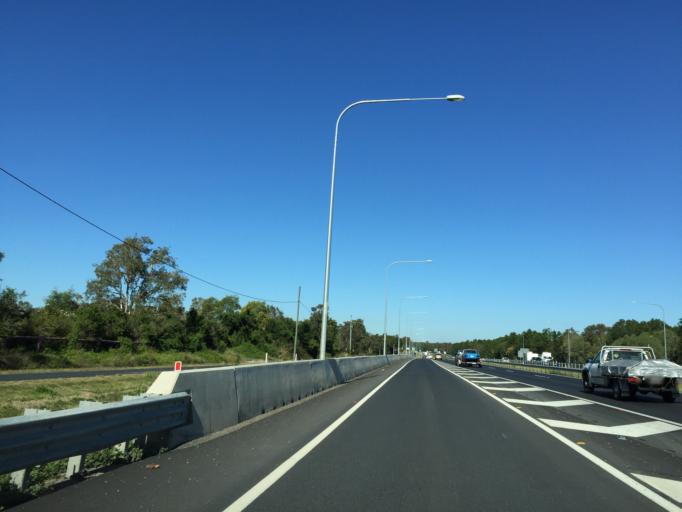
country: AU
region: Queensland
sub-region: Moreton Bay
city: Caboolture
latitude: -27.0443
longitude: 152.9779
